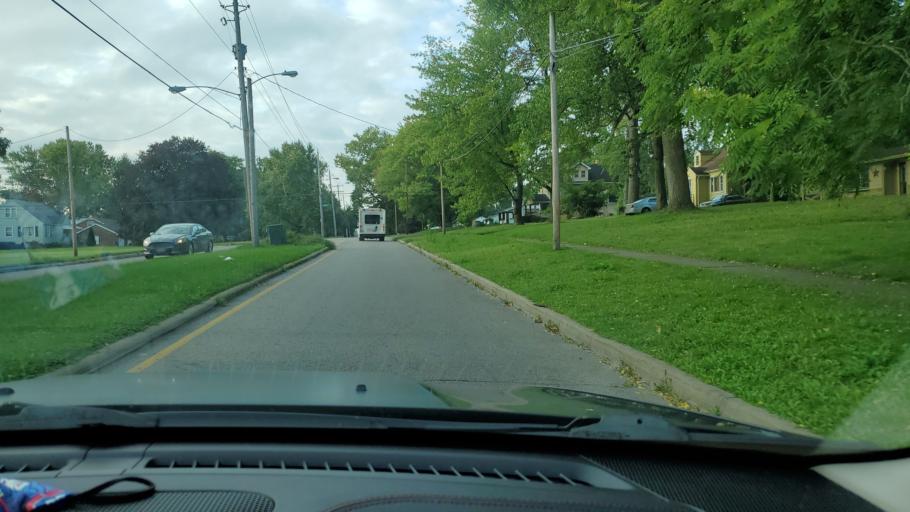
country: US
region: Ohio
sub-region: Mahoning County
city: Struthers
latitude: 41.0548
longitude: -80.6217
